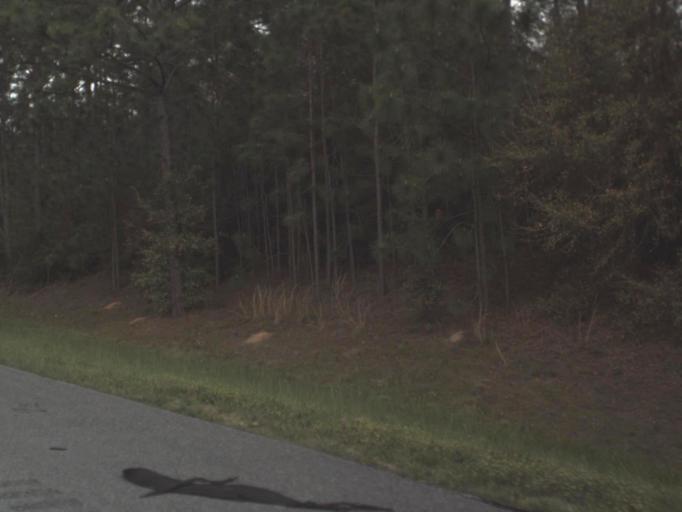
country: US
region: Florida
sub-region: Okaloosa County
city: Crestview
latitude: 30.7146
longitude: -86.6248
